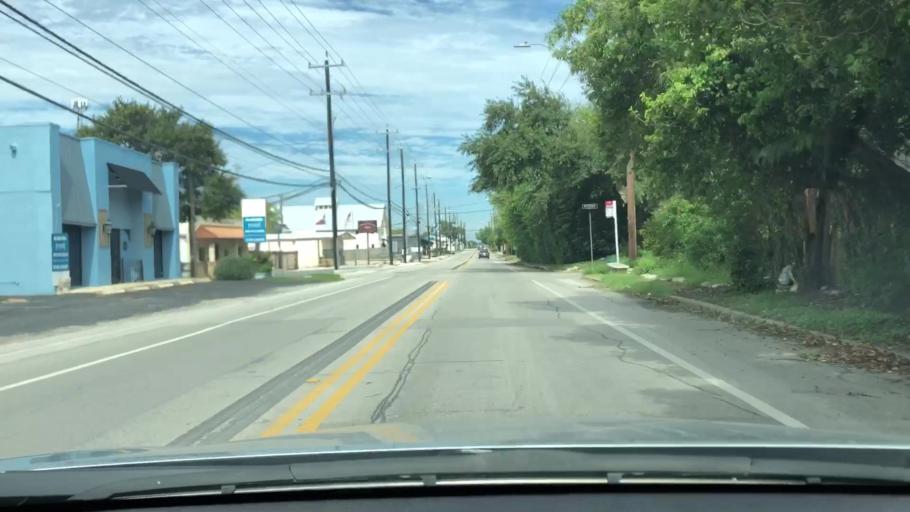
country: US
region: Texas
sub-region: Bexar County
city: Olmos Park
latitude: 29.4761
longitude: -98.4917
